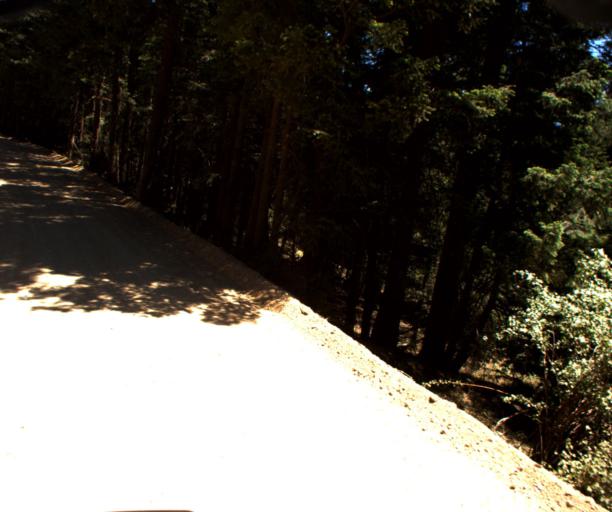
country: US
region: Arizona
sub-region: Graham County
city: Swift Trail Junction
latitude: 32.6797
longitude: -109.8914
